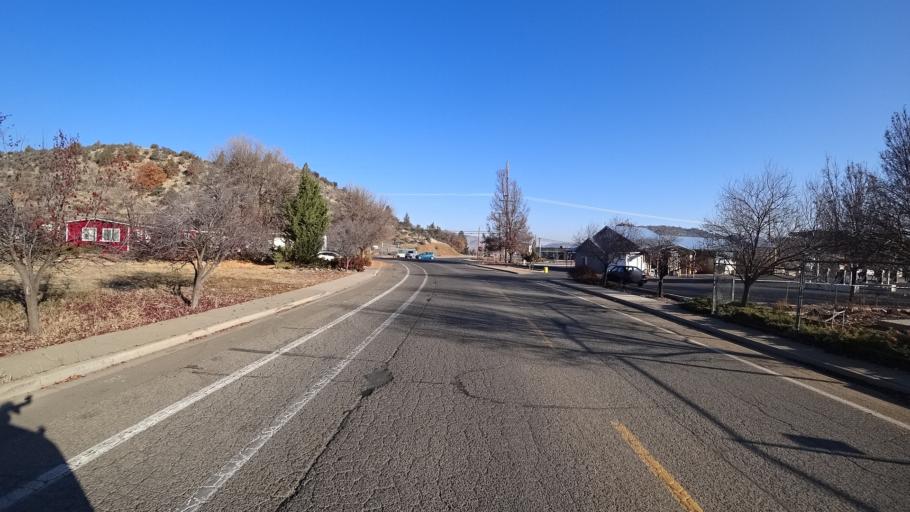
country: US
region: California
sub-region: Siskiyou County
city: Yreka
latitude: 41.7114
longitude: -122.6442
